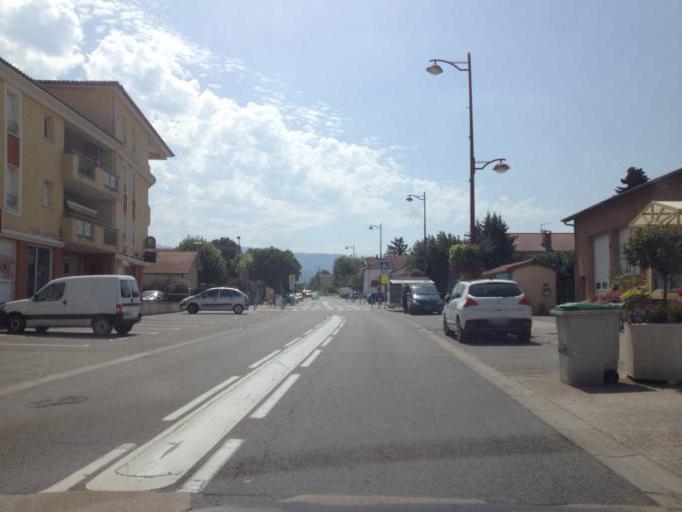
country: FR
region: Rhone-Alpes
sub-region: Departement de la Drome
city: Chatuzange-le-Goubet
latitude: 45.0062
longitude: 5.0909
